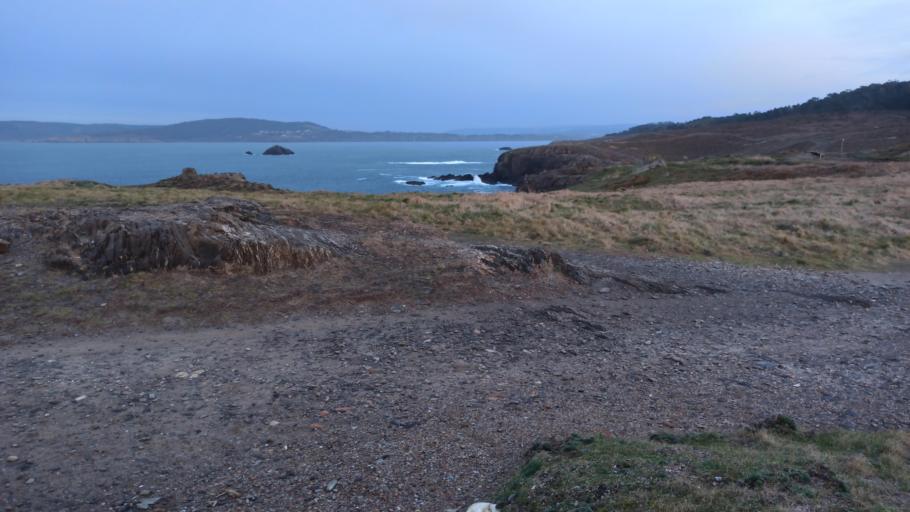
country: ES
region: Galicia
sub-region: Provincia da Coruna
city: A Coruna
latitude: 43.3958
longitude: -8.3495
